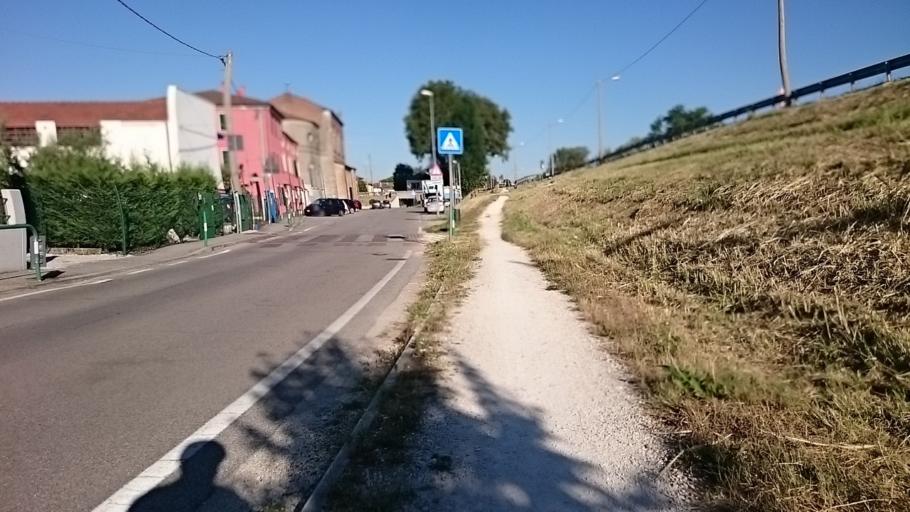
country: IT
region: Veneto
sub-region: Provincia di Padova
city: Vigodarzere
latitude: 45.4456
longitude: 11.8958
